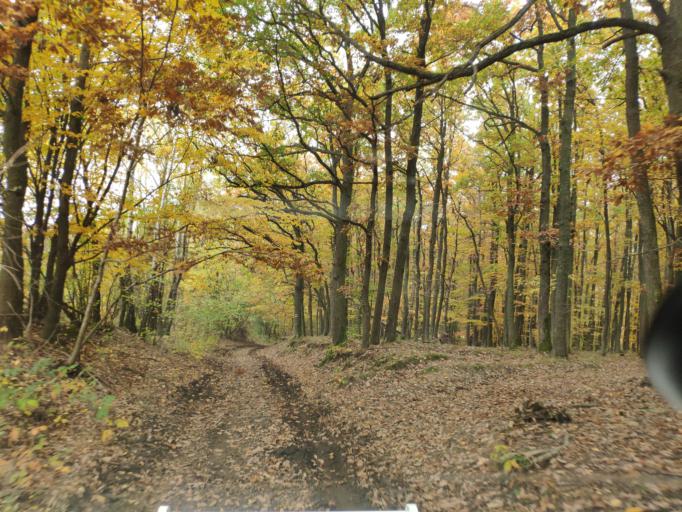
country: SK
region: Kosicky
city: Moldava nad Bodvou
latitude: 48.7170
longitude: 21.0024
